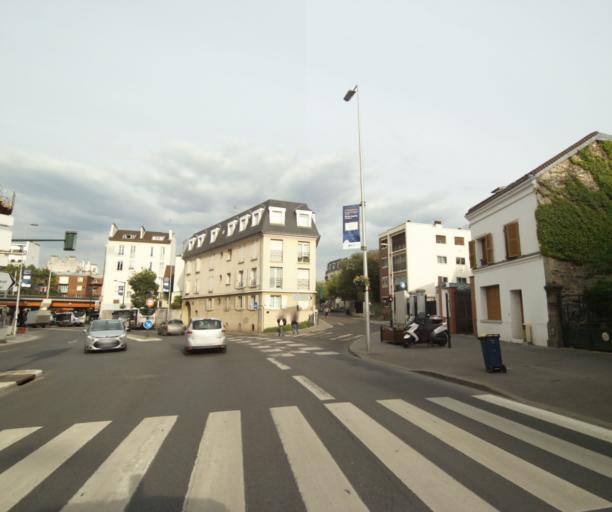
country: FR
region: Ile-de-France
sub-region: Departement des Hauts-de-Seine
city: Levallois-Perret
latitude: 48.8869
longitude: 2.3003
